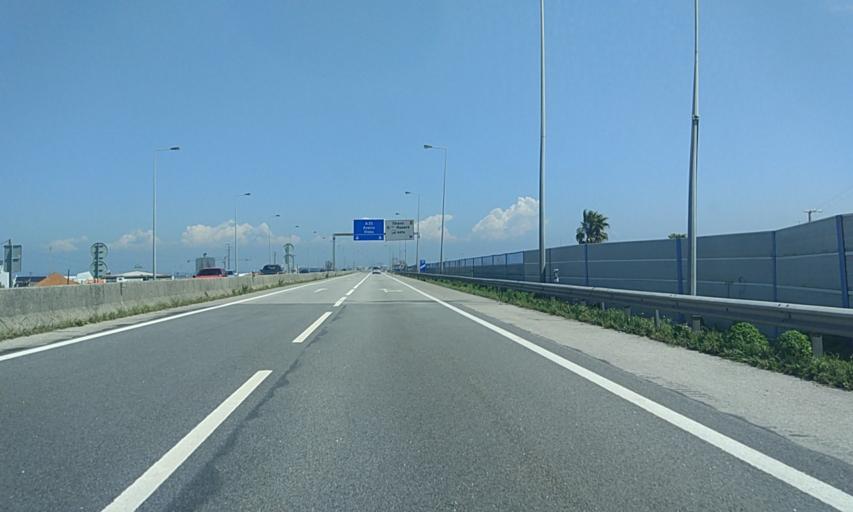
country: PT
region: Aveiro
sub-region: Ilhavo
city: Gafanha da Nazare
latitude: 40.6302
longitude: -8.6950
